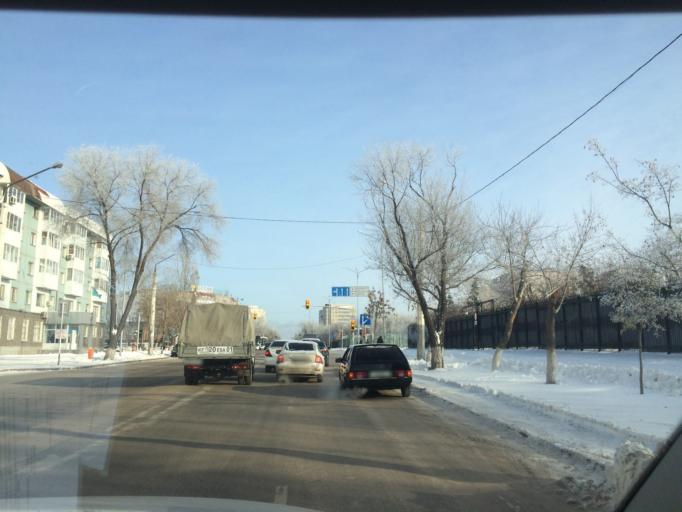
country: KZ
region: Astana Qalasy
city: Astana
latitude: 51.1709
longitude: 71.4218
